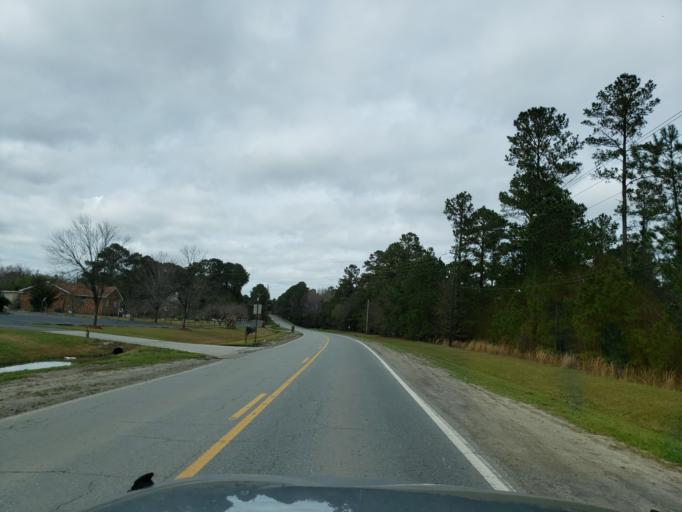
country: US
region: Georgia
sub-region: Chatham County
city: Georgetown
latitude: 32.0244
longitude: -81.2665
